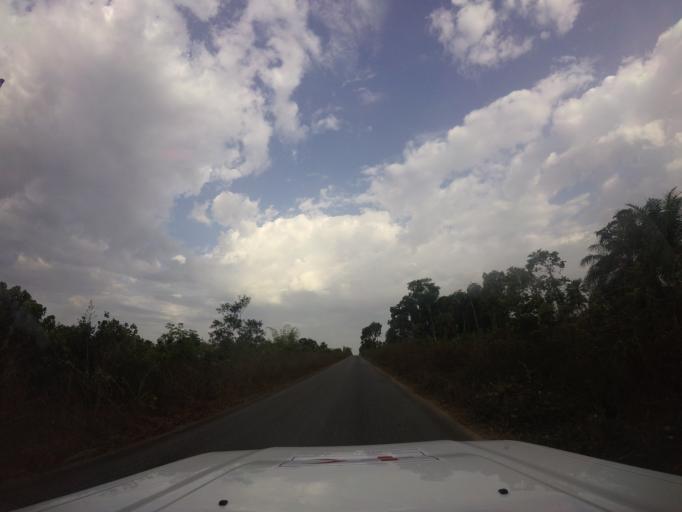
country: LR
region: Bomi
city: Tubmanburg
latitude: 6.7076
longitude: -10.9280
